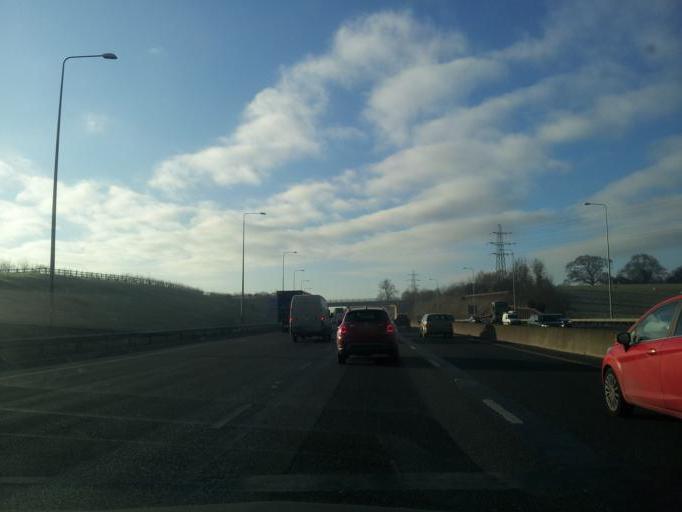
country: GB
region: England
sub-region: Buckinghamshire
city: Chalfont Saint Peter
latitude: 51.6257
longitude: -0.5227
